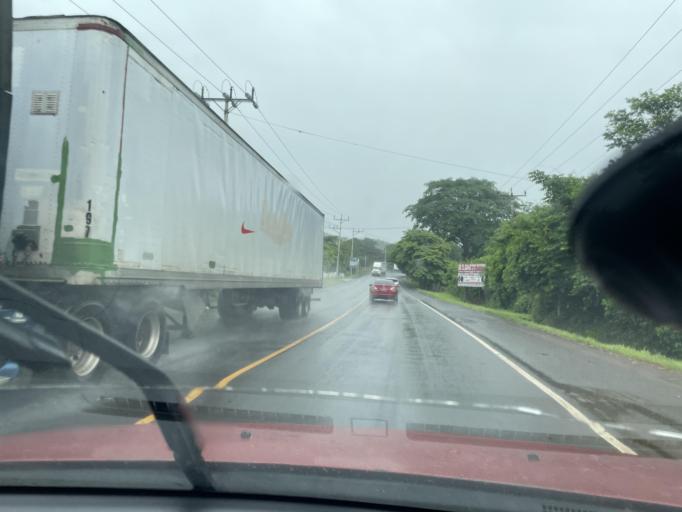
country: SV
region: Morazan
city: Jocoro
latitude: 13.5715
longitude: -88.0882
